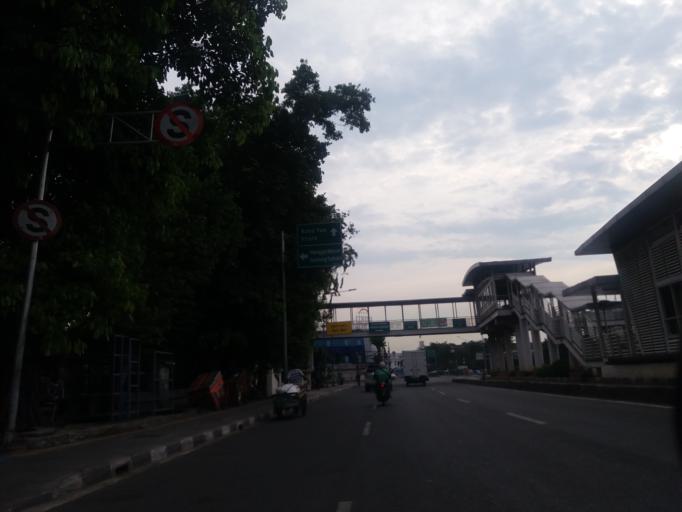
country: ID
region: Jakarta Raya
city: Jakarta
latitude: -6.1377
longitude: 106.8180
